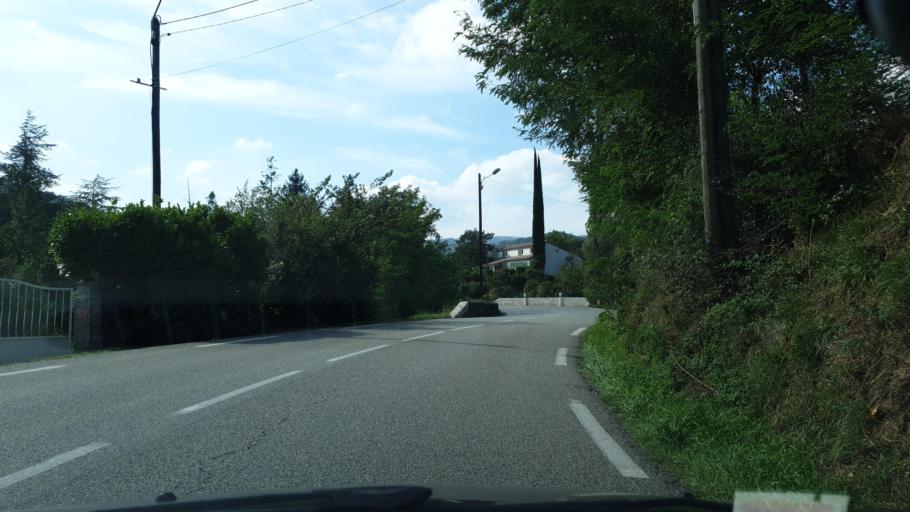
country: FR
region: Rhone-Alpes
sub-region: Departement de l'Ardeche
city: Saint-Sauveur-de-Montagut
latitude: 44.8095
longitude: 4.6301
